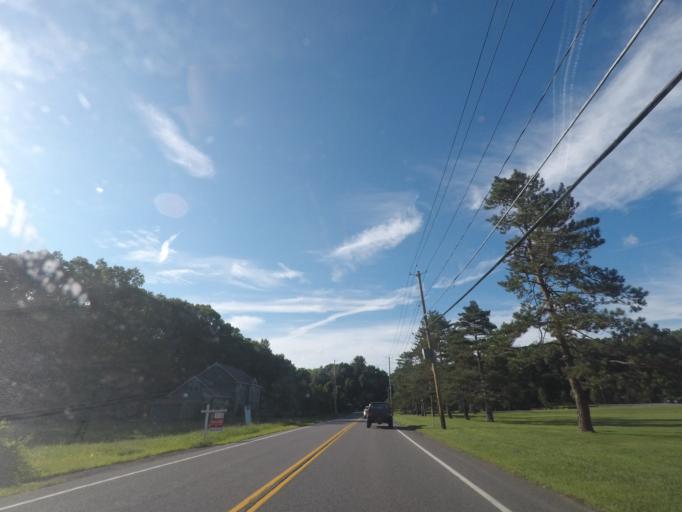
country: US
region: New York
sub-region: Albany County
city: West Albany
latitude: 42.7197
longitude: -73.7697
